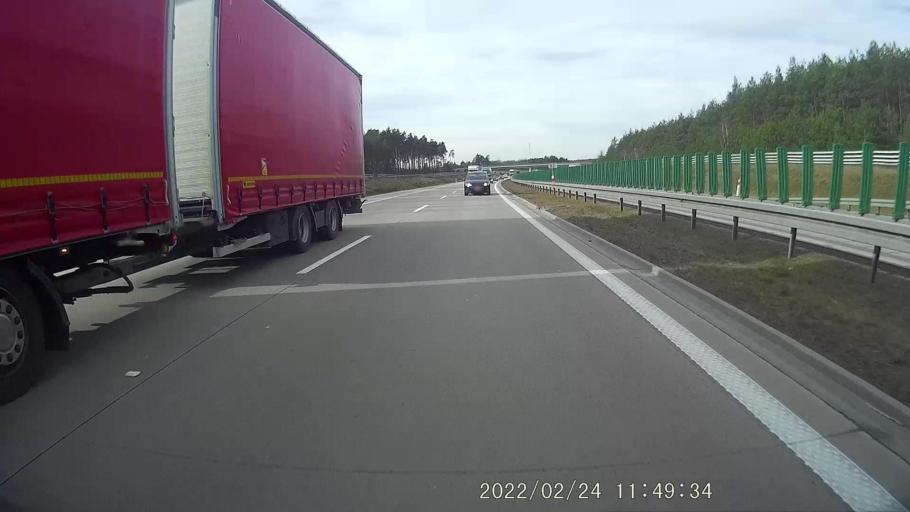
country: PL
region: Lower Silesian Voivodeship
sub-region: Powiat polkowicki
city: Radwanice
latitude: 51.5967
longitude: 15.9606
